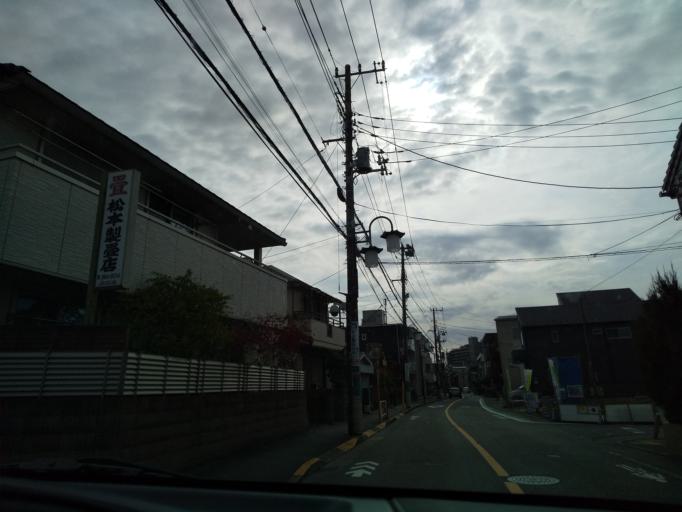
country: JP
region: Tokyo
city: Kokubunji
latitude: 35.6614
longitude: 139.4534
